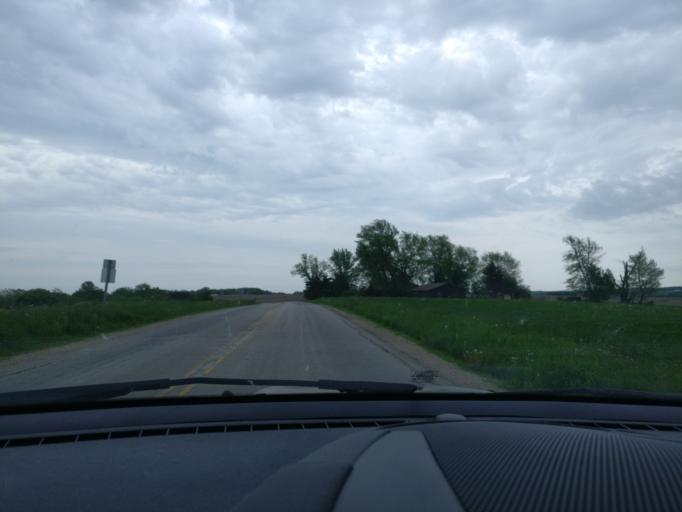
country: US
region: Wisconsin
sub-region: Lafayette County
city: Darlington
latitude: 42.7510
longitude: -90.0035
